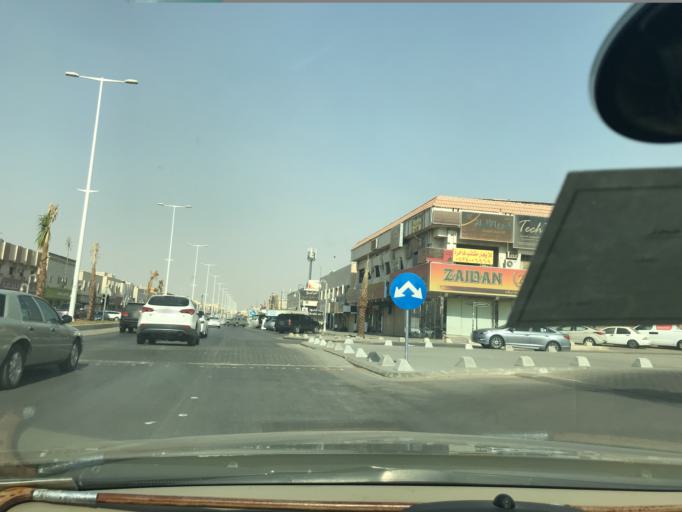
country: SA
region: Ar Riyad
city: Riyadh
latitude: 24.7479
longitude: 46.7617
